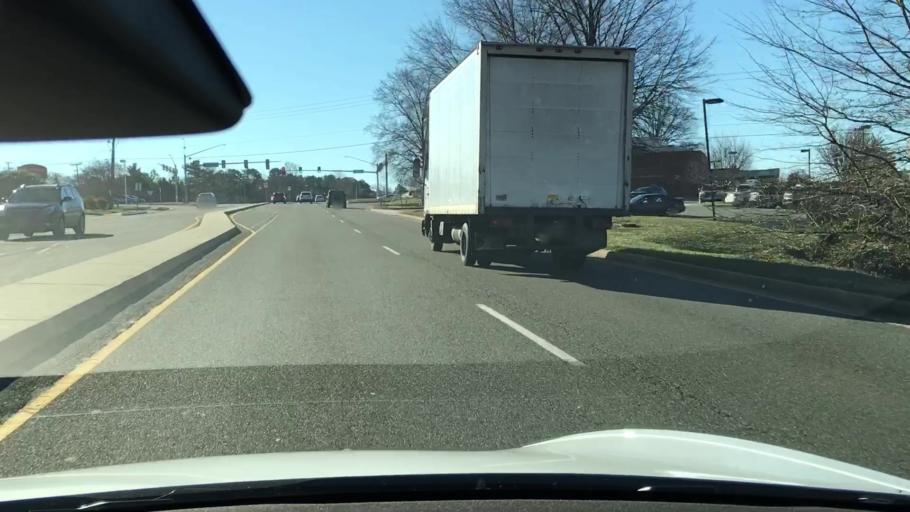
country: US
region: Virginia
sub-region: Henrico County
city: Tuckahoe
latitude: 37.6032
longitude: -77.5644
